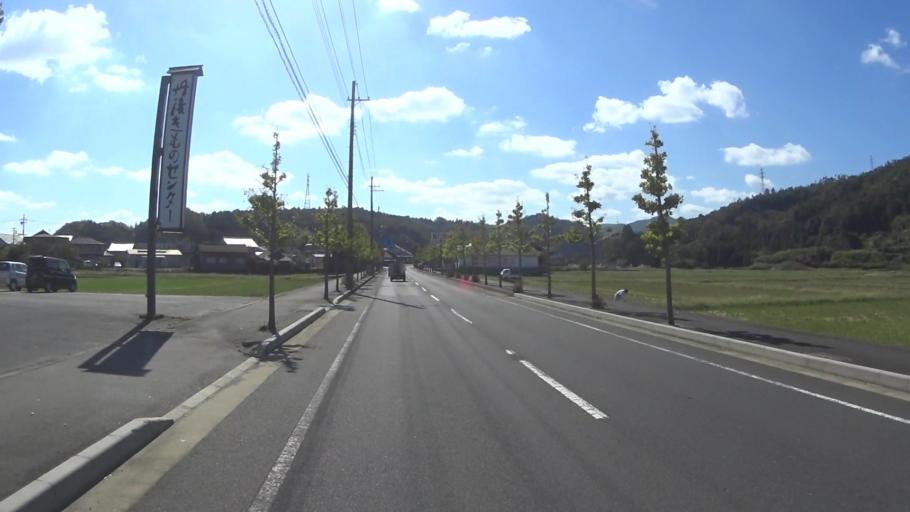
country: JP
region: Kyoto
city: Miyazu
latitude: 35.6693
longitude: 135.0250
